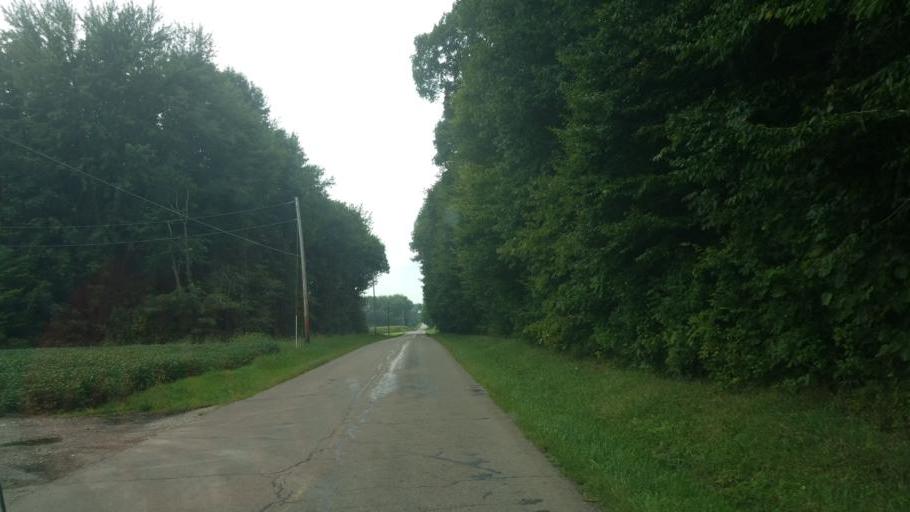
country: US
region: Ohio
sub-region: Wayne County
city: Wooster
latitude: 40.9011
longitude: -81.9607
